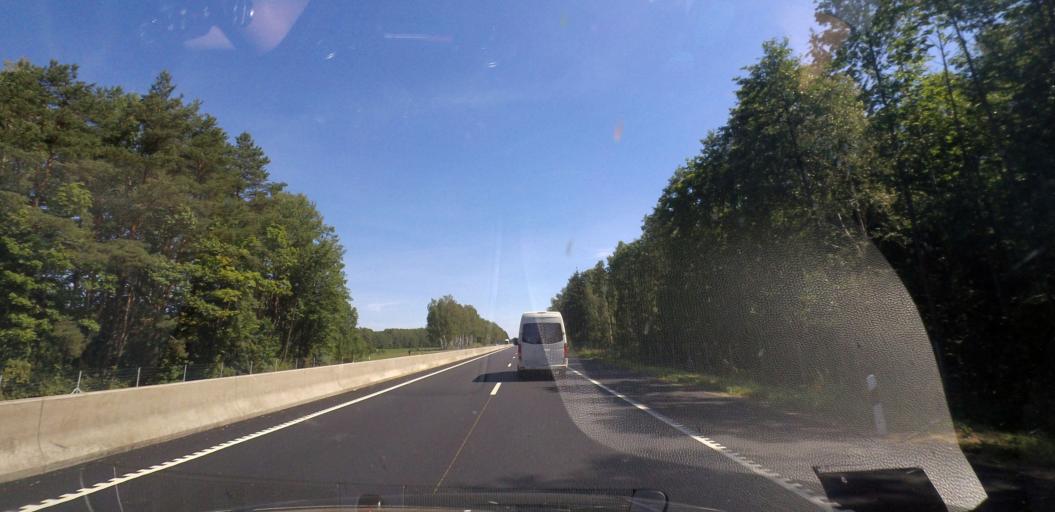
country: BY
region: Grodnenskaya
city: Lida
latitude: 53.7722
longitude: 25.0548
